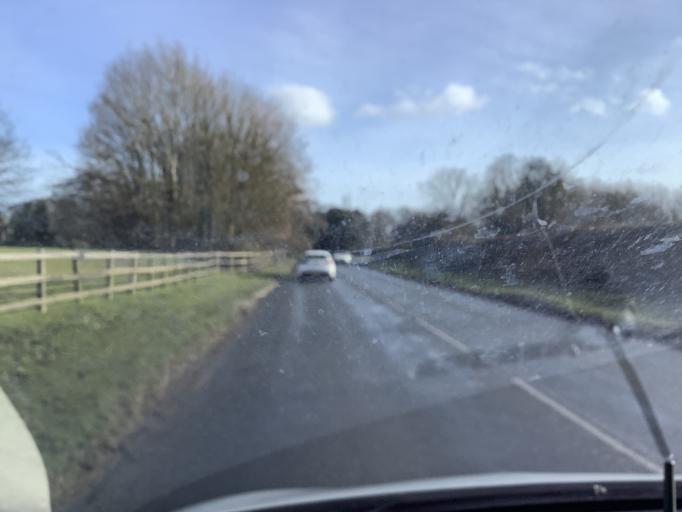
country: GB
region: England
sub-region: Hampshire
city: Hythe
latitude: 50.8172
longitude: -1.4540
